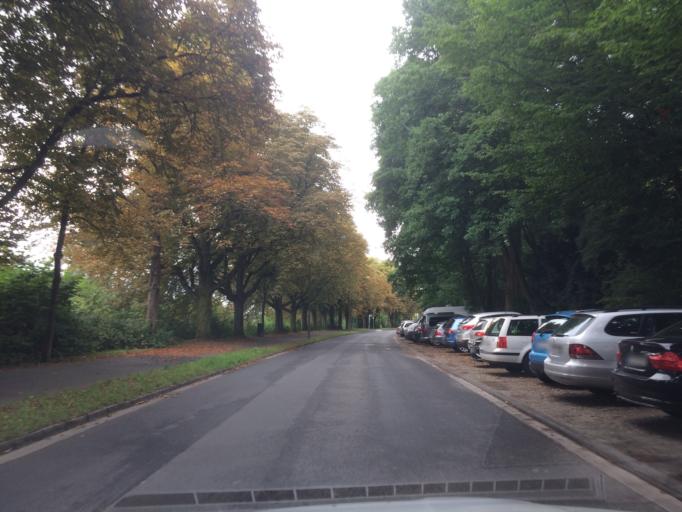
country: DE
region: Hesse
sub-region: Regierungsbezirk Kassel
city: Kassel
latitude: 51.3069
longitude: 9.5018
